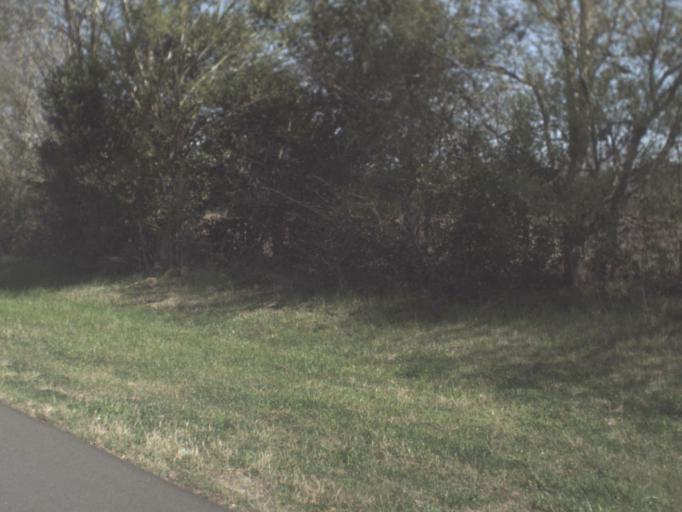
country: US
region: Florida
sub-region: Jackson County
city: Sneads
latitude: 30.7783
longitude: -85.0189
